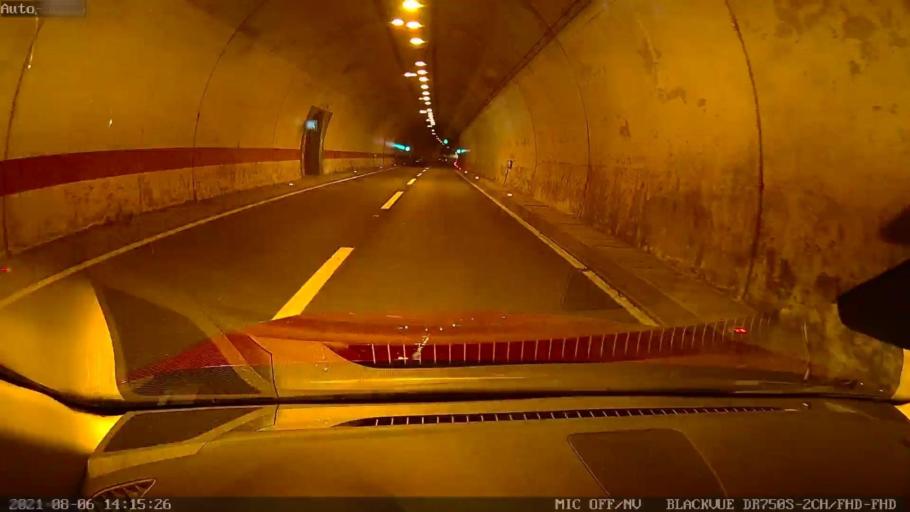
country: HR
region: Primorsko-Goranska
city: Vrbovsko
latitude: 45.3754
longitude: 14.9688
